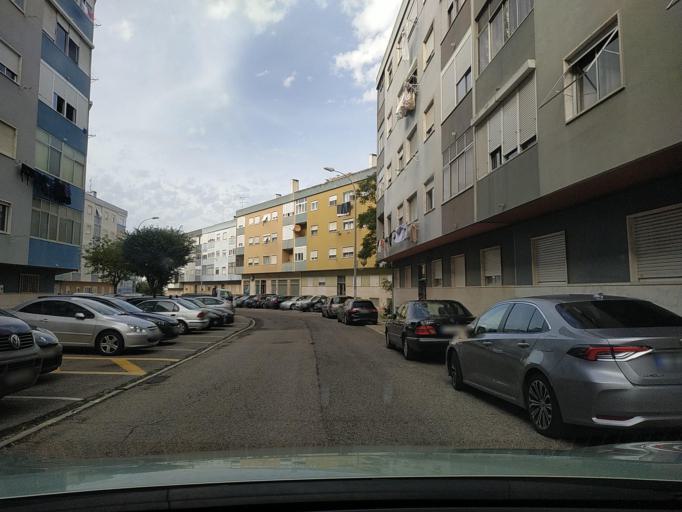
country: PT
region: Lisbon
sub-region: Amadora
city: Amadora
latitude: 38.7657
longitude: -9.2328
